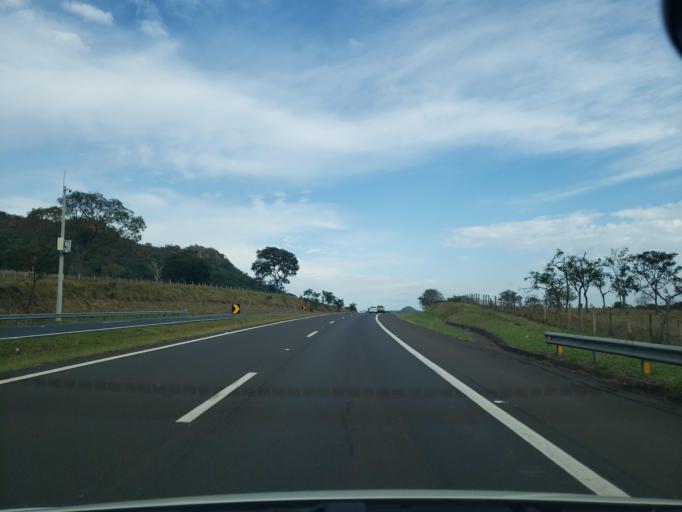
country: BR
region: Sao Paulo
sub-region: Itirapina
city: Itirapina
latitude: -22.2743
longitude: -47.9469
